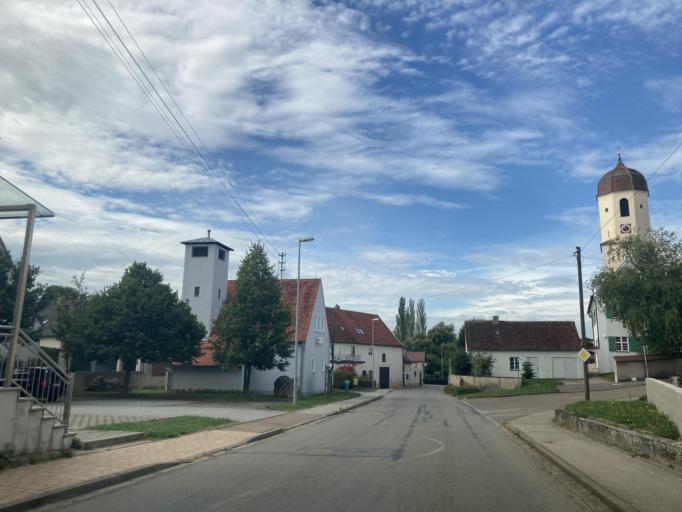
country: DE
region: Bavaria
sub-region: Swabia
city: Mottingen
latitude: 48.8180
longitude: 10.6064
